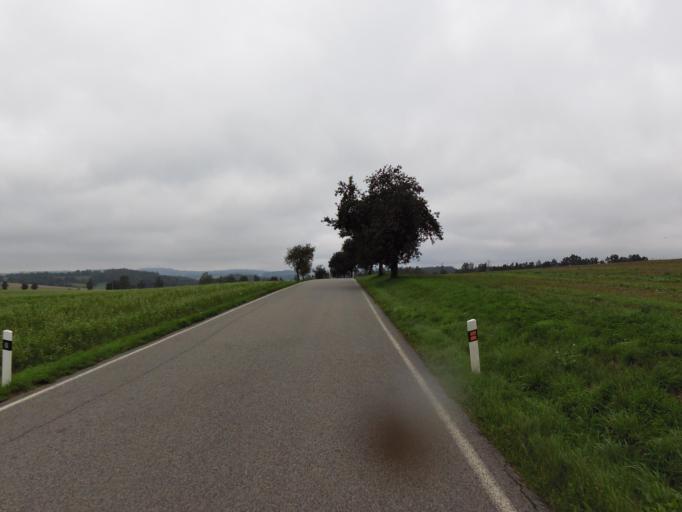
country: CZ
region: Jihocesky
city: Mlada Vozice
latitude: 49.5820
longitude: 14.7538
